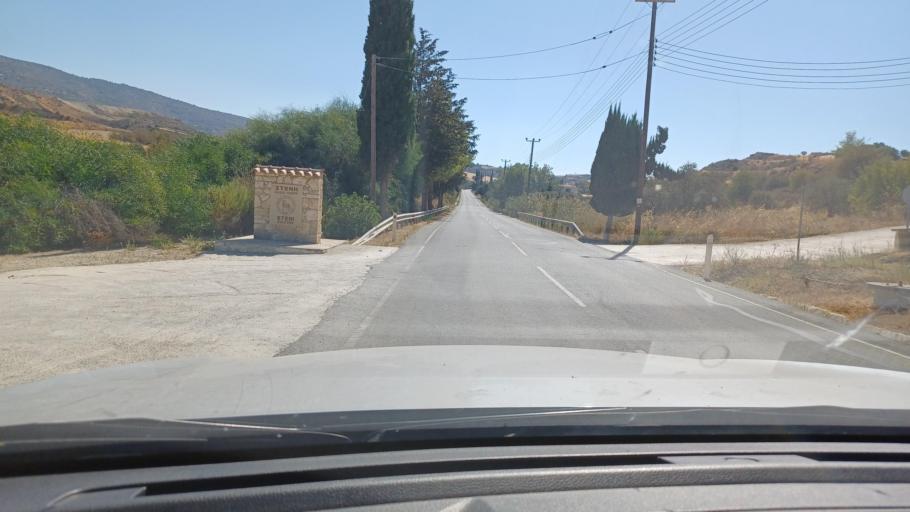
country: CY
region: Pafos
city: Polis
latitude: 35.0198
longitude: 32.4465
